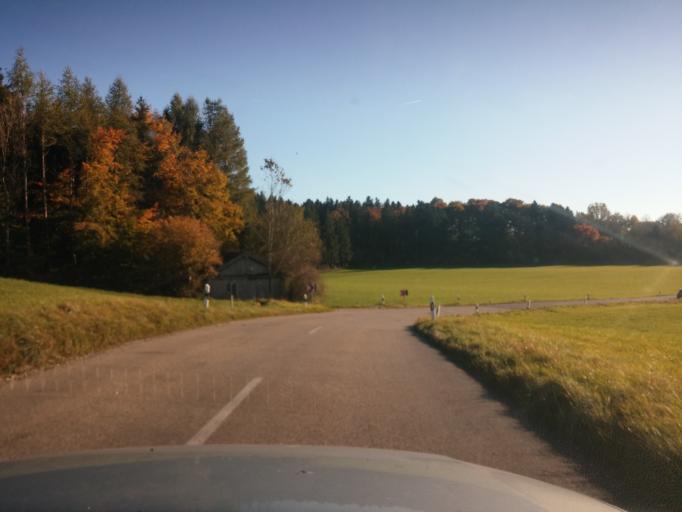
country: DE
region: Bavaria
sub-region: Upper Bavaria
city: Aying
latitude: 47.9796
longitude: 11.7830
